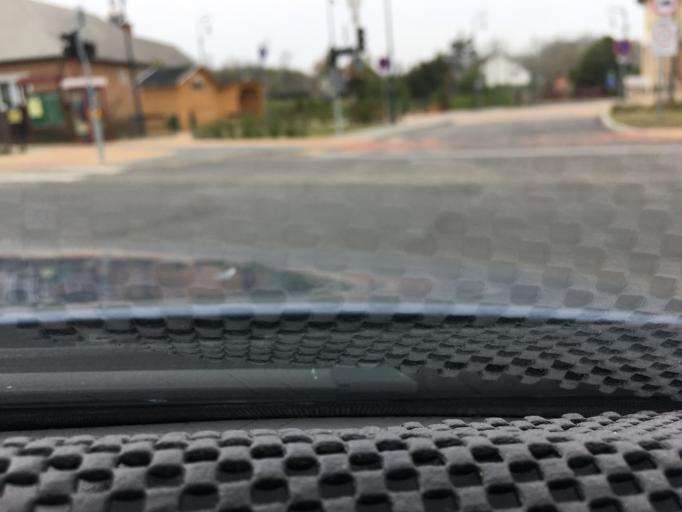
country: HU
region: Hajdu-Bihar
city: Nyiradony
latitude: 47.6902
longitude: 21.9038
